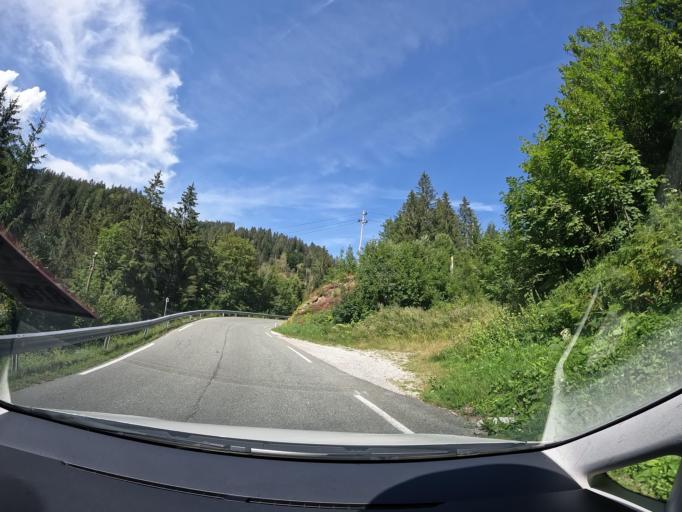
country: AT
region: Carinthia
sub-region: Politischer Bezirk Villach Land
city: Sankt Jakob
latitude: 46.5520
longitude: 14.0796
